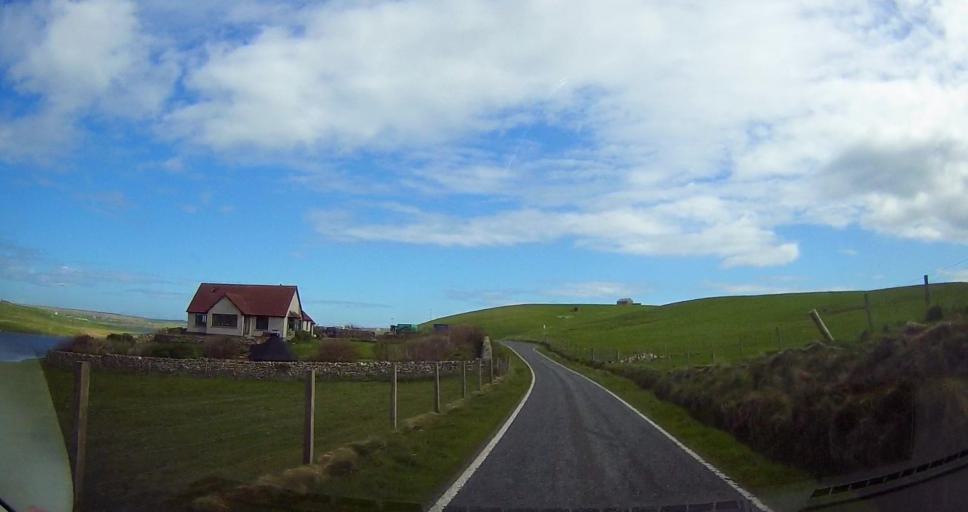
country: GB
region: Scotland
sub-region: Shetland Islands
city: Sandwick
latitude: 59.9255
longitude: -1.3422
